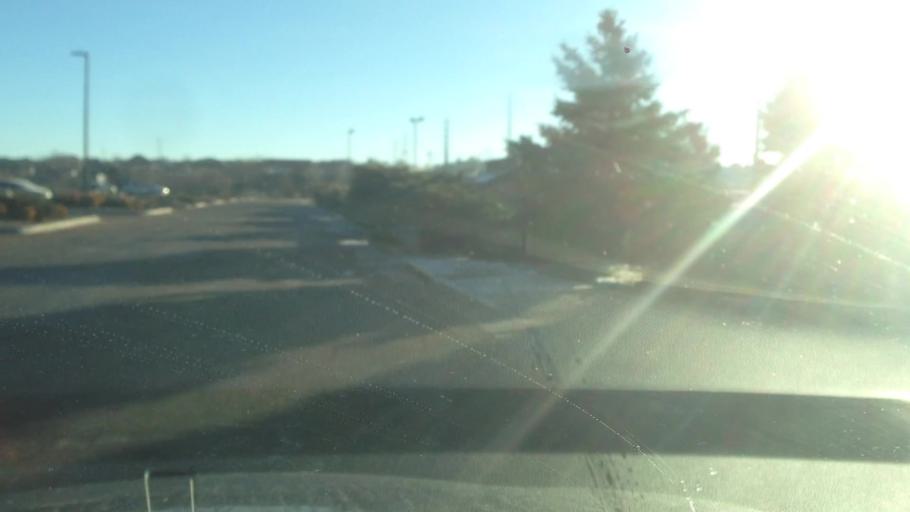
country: US
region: Colorado
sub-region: Douglas County
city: Parker
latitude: 39.5119
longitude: -104.7690
